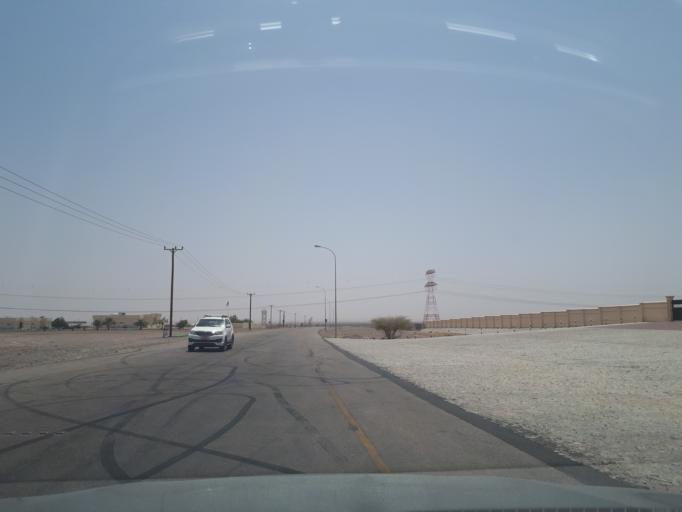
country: OM
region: Ash Sharqiyah
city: Badiyah
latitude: 22.4640
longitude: 59.0519
